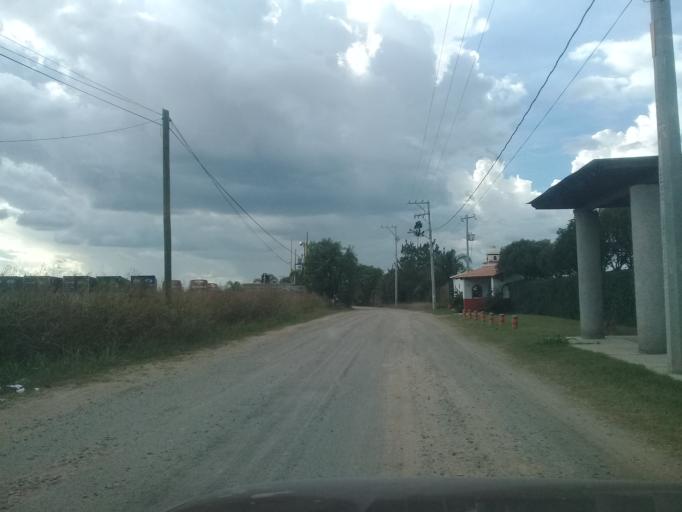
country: MX
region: Aguascalientes
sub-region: Aguascalientes
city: San Sebastian [Fraccionamiento]
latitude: 21.7802
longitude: -102.2836
